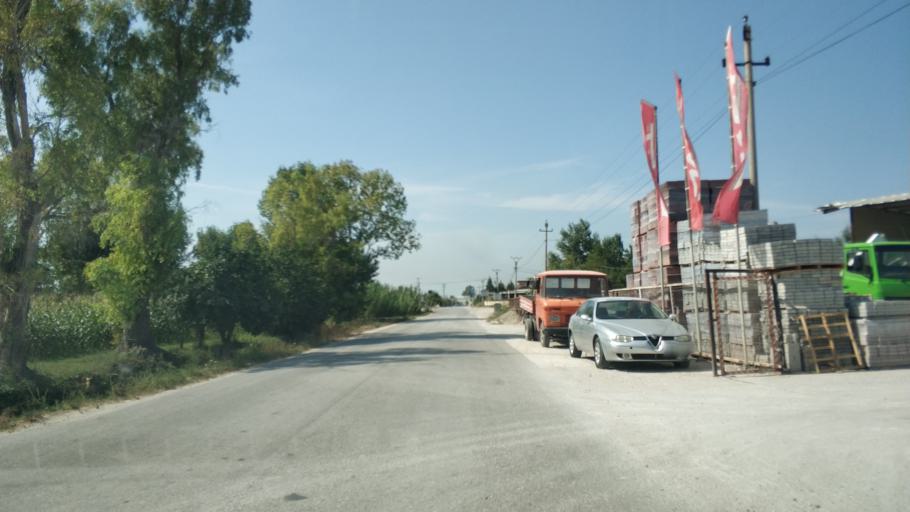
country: AL
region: Fier
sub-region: Rrethi i Fierit
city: Dermenas
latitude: 40.7408
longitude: 19.5077
